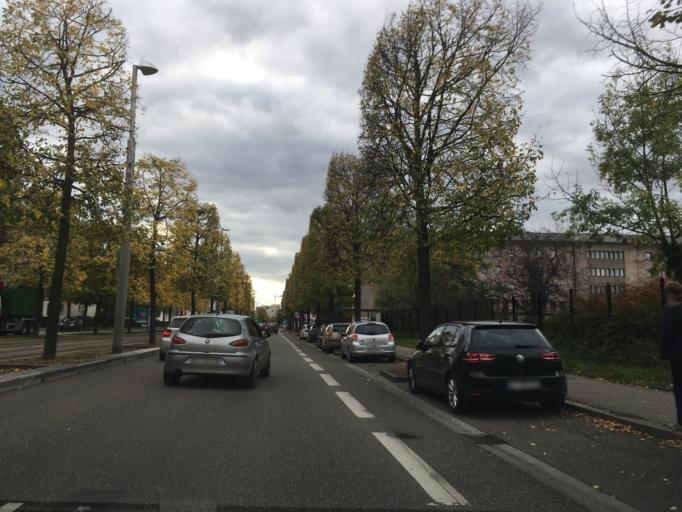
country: FR
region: Alsace
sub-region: Departement du Bas-Rhin
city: Strasbourg
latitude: 48.5600
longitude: 7.7503
